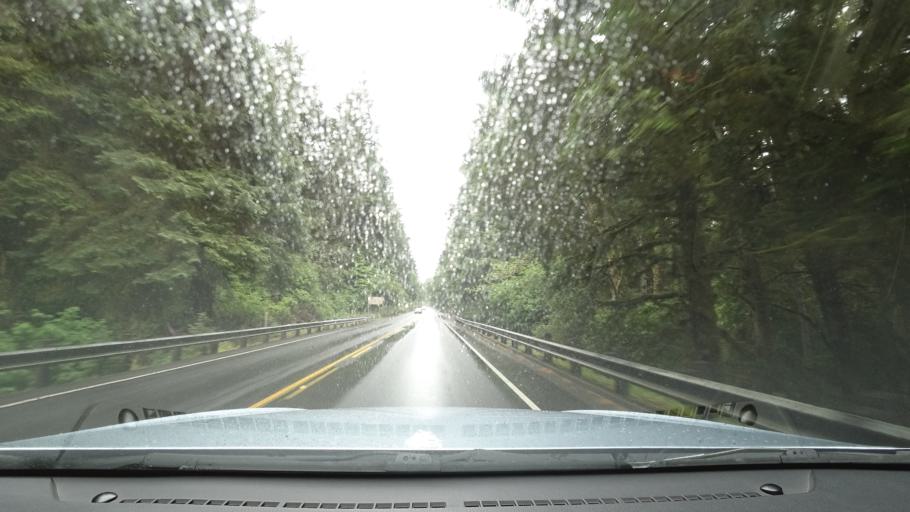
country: US
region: Oregon
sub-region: Lane County
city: Dunes City
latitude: 43.8804
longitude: -124.1304
